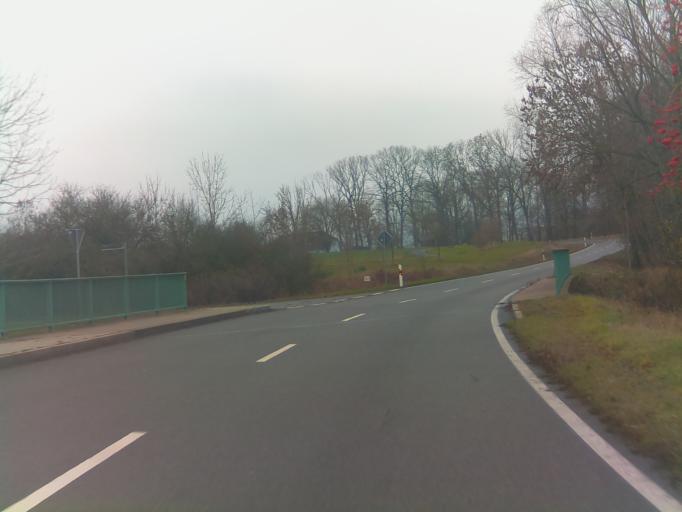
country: DE
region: Thuringia
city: Romhild
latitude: 50.4164
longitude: 10.5333
